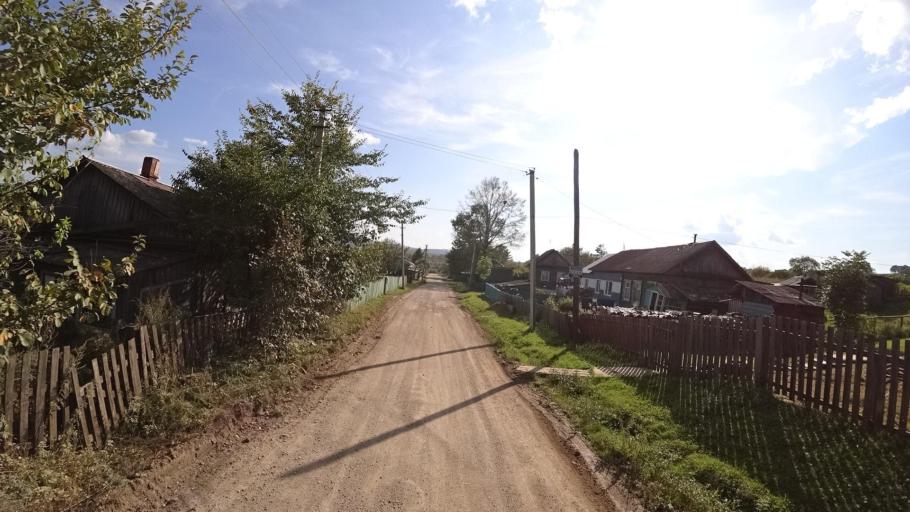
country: RU
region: Jewish Autonomous Oblast
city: Birakan
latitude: 48.9972
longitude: 131.7253
